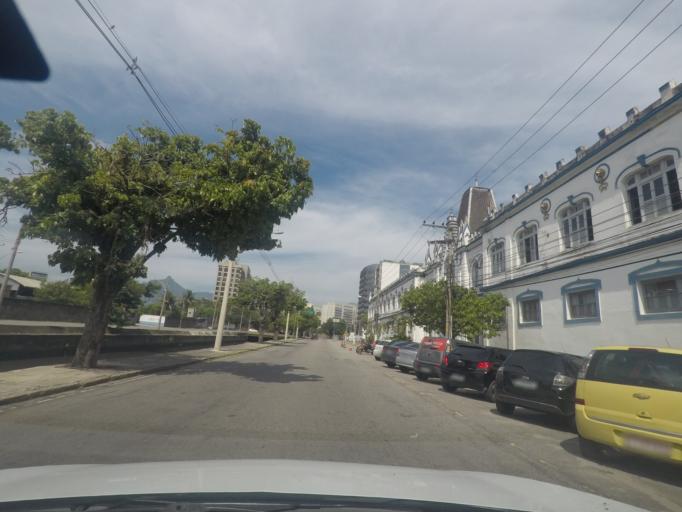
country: BR
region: Rio de Janeiro
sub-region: Rio De Janeiro
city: Rio de Janeiro
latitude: -22.9071
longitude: -43.2165
